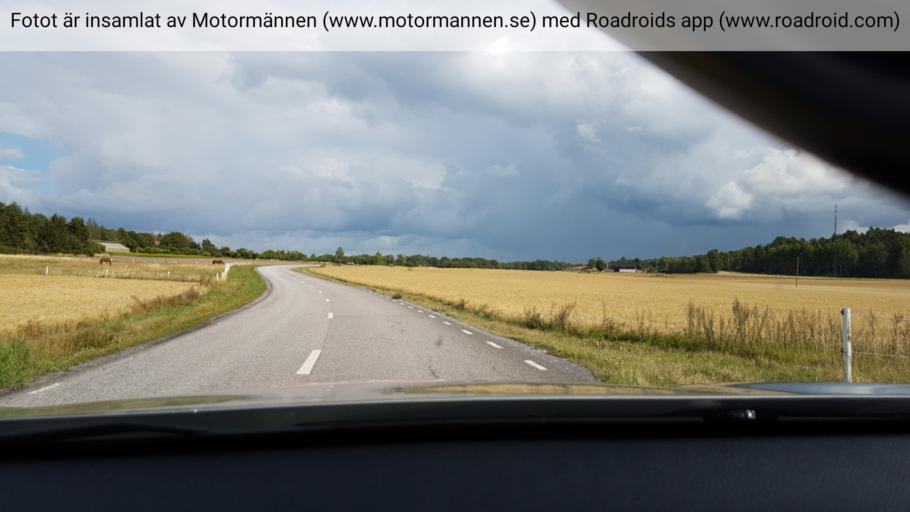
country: SE
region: Stockholm
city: Stenhamra
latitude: 59.3903
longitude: 17.6664
